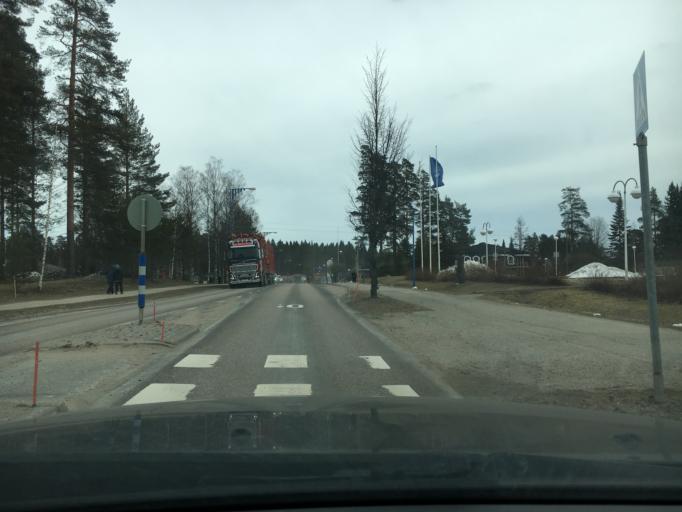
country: FI
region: Central Finland
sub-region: AEaenekoski
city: Konnevesi
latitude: 62.6281
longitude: 26.2857
